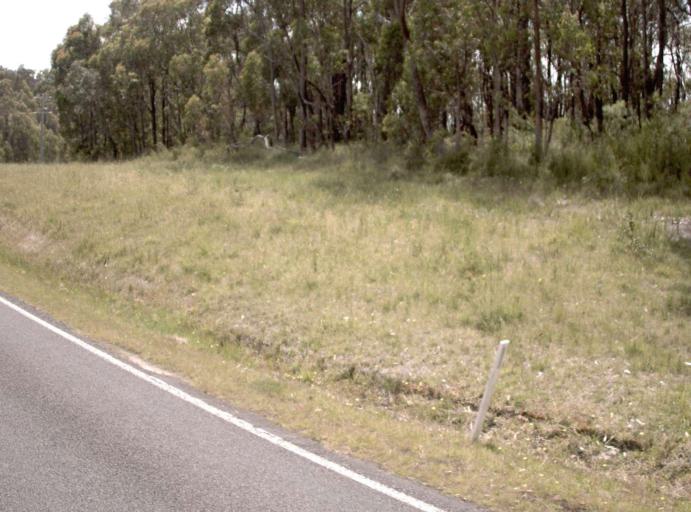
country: AU
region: Victoria
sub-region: Latrobe
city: Moe
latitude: -38.0470
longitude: 146.3232
